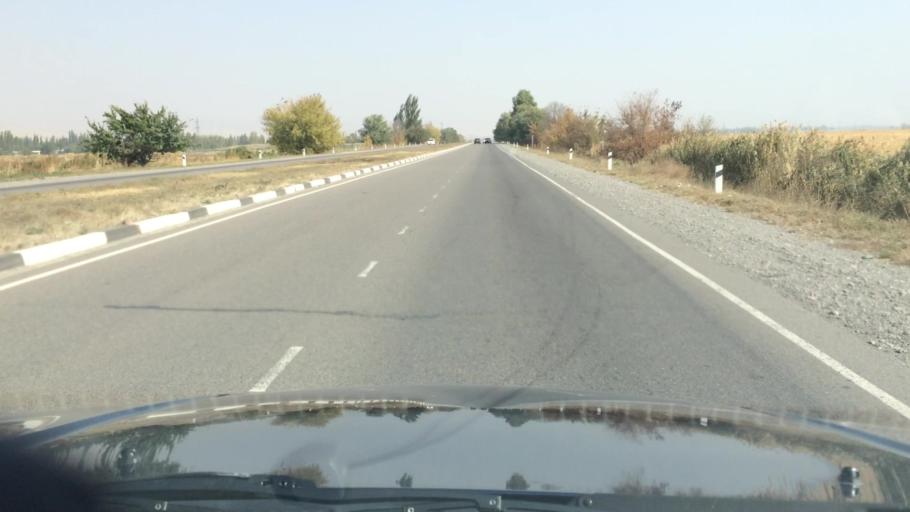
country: KG
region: Chuy
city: Kant
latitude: 42.9571
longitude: 74.7970
